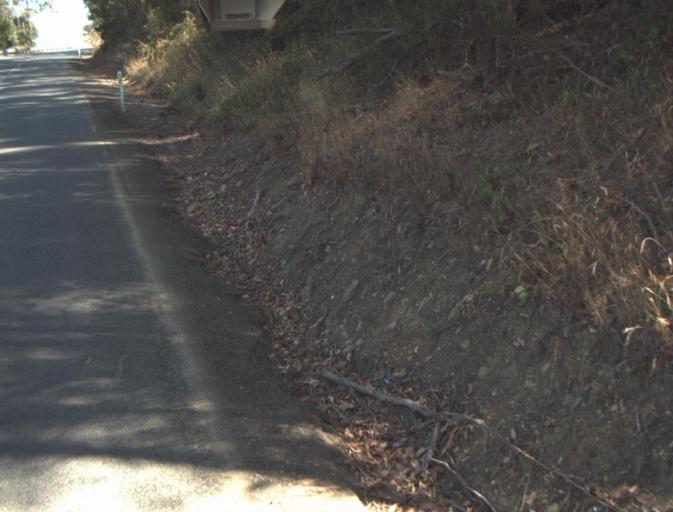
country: AU
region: Tasmania
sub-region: Launceston
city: Mayfield
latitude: -41.2230
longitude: 147.2070
